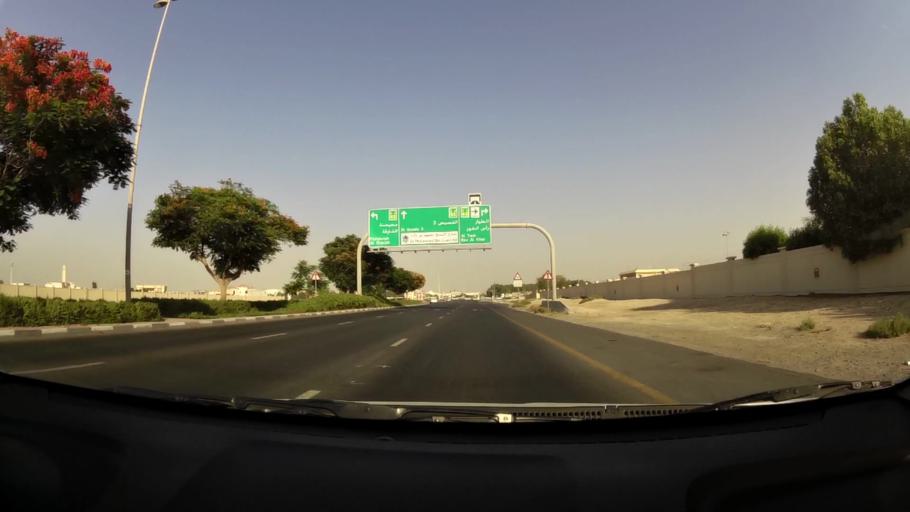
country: AE
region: Ash Shariqah
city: Sharjah
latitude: 25.2726
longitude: 55.3934
